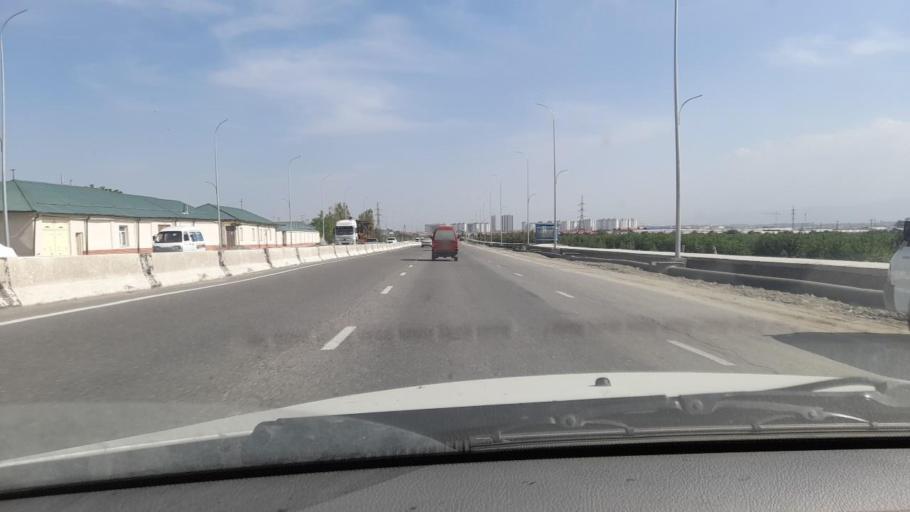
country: UZ
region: Samarqand
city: Daxbet
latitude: 39.7449
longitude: 66.9243
